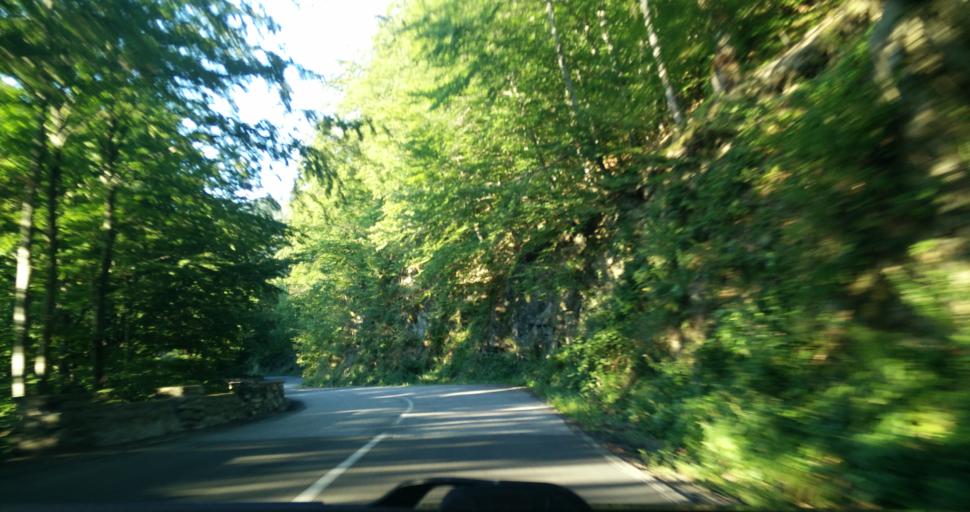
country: RO
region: Bihor
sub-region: Oras Nucet
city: Nucet
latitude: 46.4822
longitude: 22.5970
